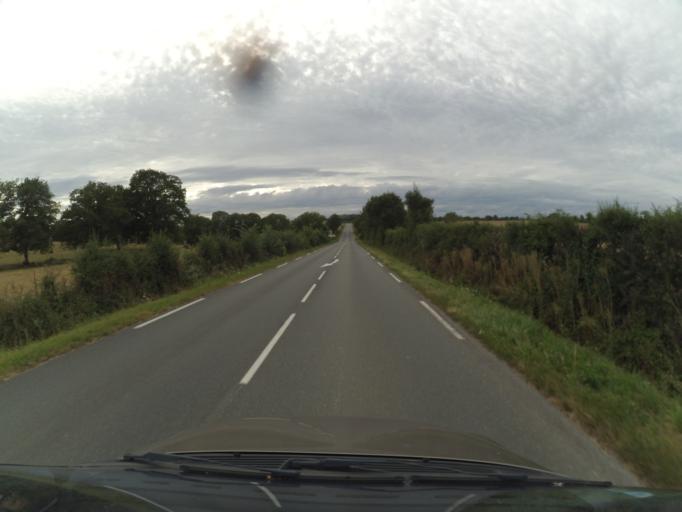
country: FR
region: Pays de la Loire
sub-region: Departement de la Vendee
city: Saint-Aubin-des-Ormeaux
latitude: 47.0171
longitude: -1.0048
